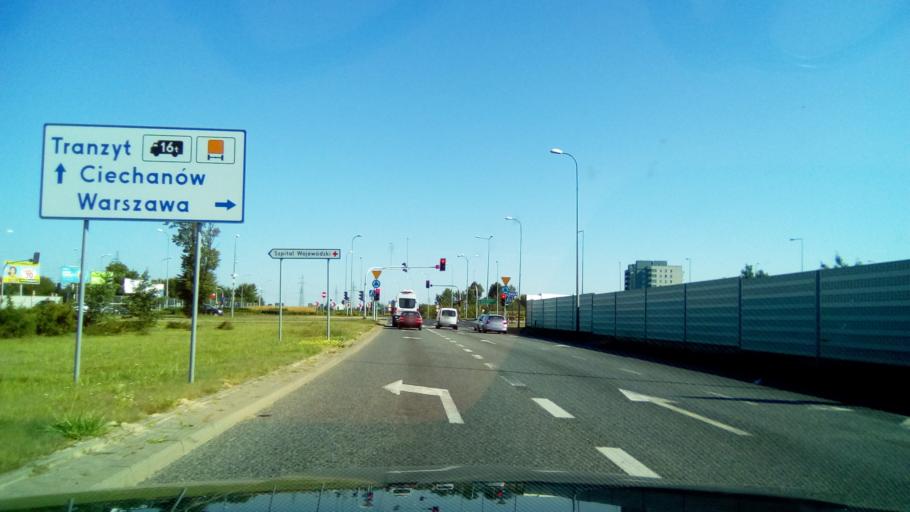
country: PL
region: Masovian Voivodeship
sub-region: Plock
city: Plock
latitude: 52.5375
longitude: 19.7429
